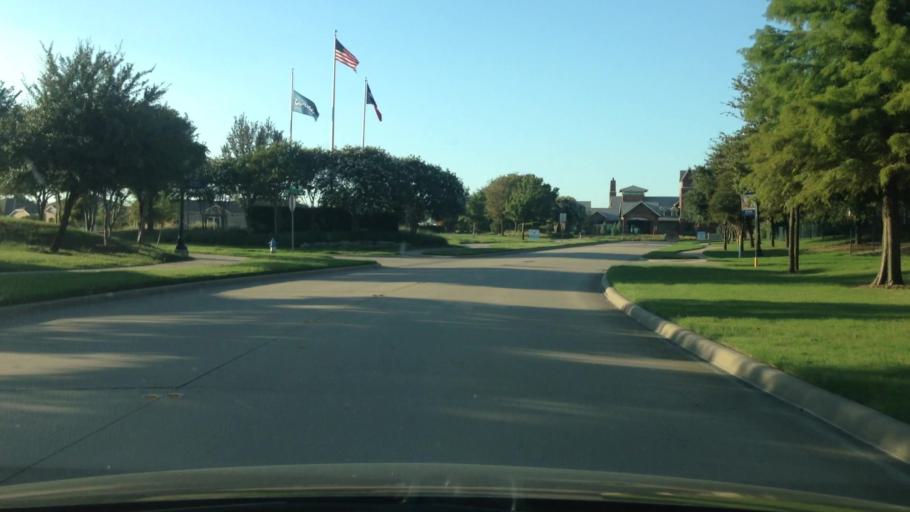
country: US
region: Texas
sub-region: Denton County
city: Little Elm
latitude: 33.1379
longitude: -96.8980
